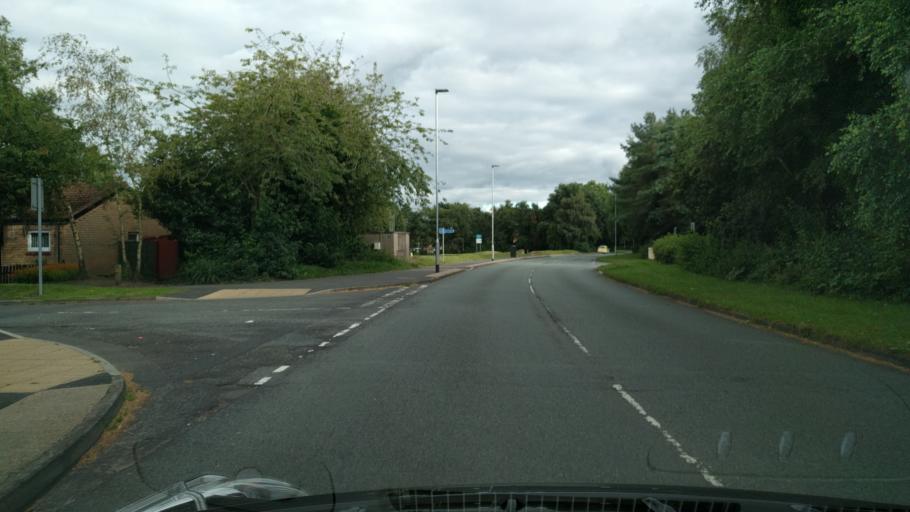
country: GB
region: England
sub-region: Warrington
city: Croft
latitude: 53.4190
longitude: -2.5235
